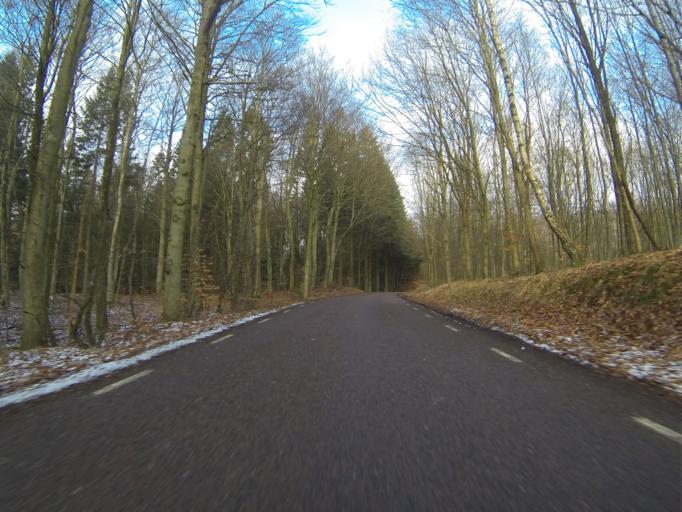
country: SE
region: Skane
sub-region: Svedala Kommun
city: Svedala
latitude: 55.5296
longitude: 13.2756
